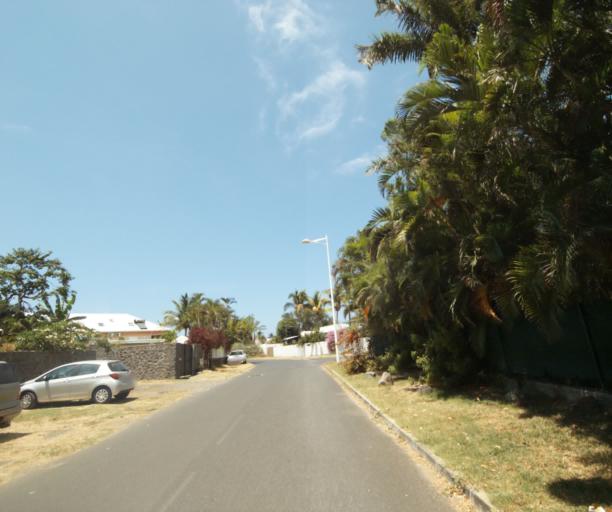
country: RE
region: Reunion
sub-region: Reunion
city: Trois-Bassins
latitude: -21.0798
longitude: 55.2283
